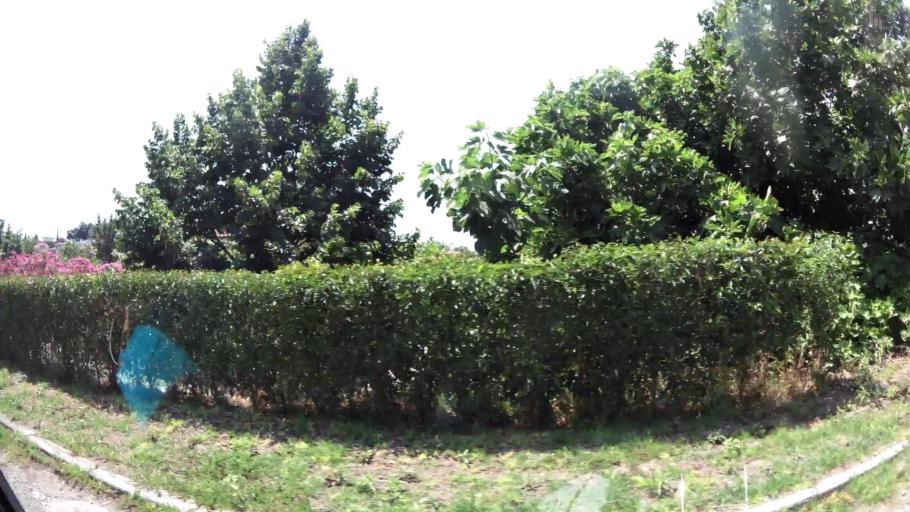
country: GR
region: Central Macedonia
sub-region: Nomos Thessalonikis
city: Trilofos
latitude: 40.4650
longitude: 22.9743
